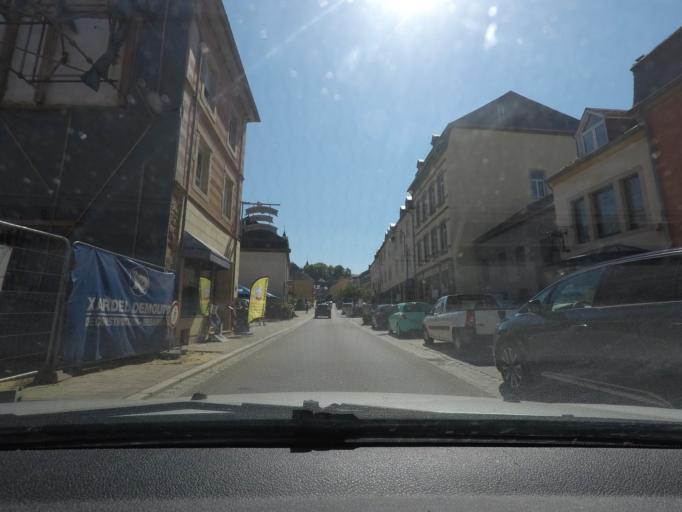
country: LU
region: Diekirch
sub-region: Canton de Redange
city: Redange-sur-Attert
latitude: 49.7642
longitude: 5.8848
